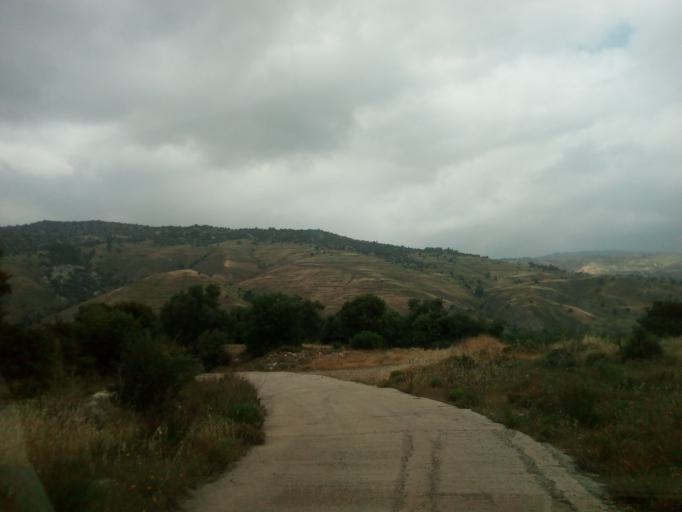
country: CY
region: Limassol
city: Pissouri
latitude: 34.8142
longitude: 32.6281
